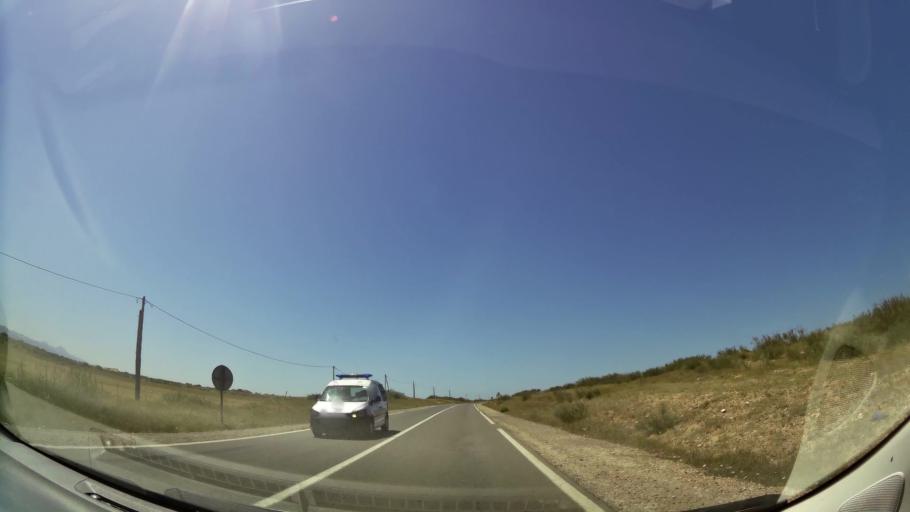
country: MA
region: Oriental
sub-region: Berkane-Taourirt
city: Madagh
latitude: 35.1268
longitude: -2.3913
